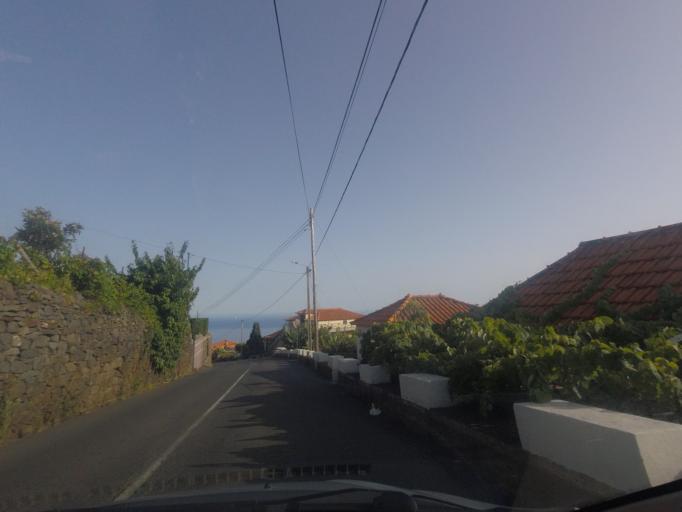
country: PT
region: Madeira
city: Ponta do Sol
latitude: 32.6943
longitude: -17.1117
